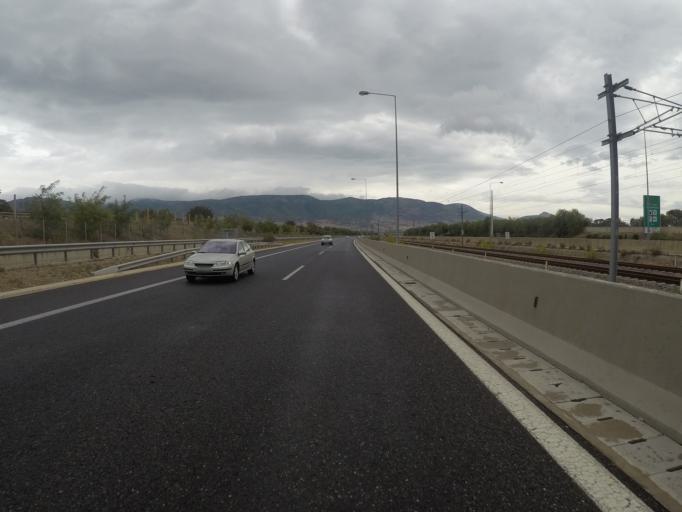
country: GR
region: Attica
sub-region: Nomarchia Dytikis Attikis
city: Magoula
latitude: 38.0877
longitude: 23.5458
